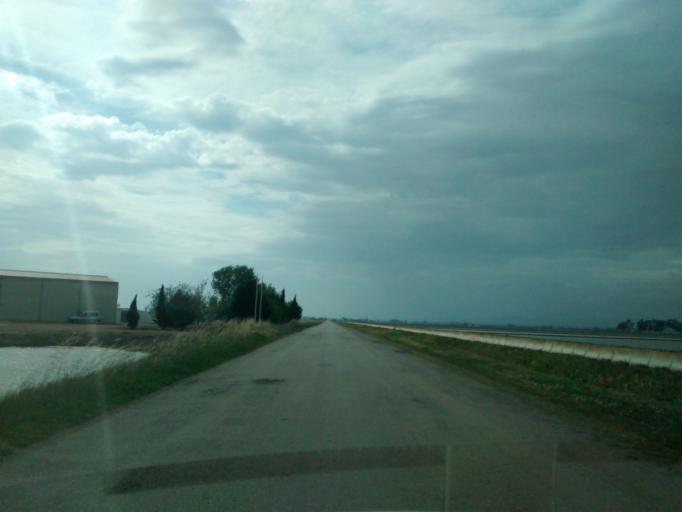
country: ES
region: Catalonia
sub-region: Provincia de Tarragona
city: Deltebre
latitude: 40.6934
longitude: 0.7706
